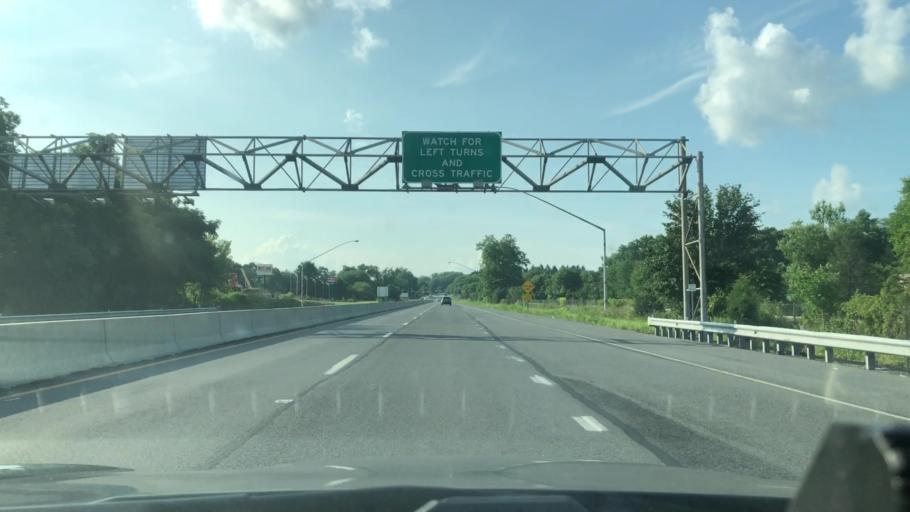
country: US
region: Pennsylvania
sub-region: Lehigh County
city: Wescosville
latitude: 40.6027
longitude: -75.5614
